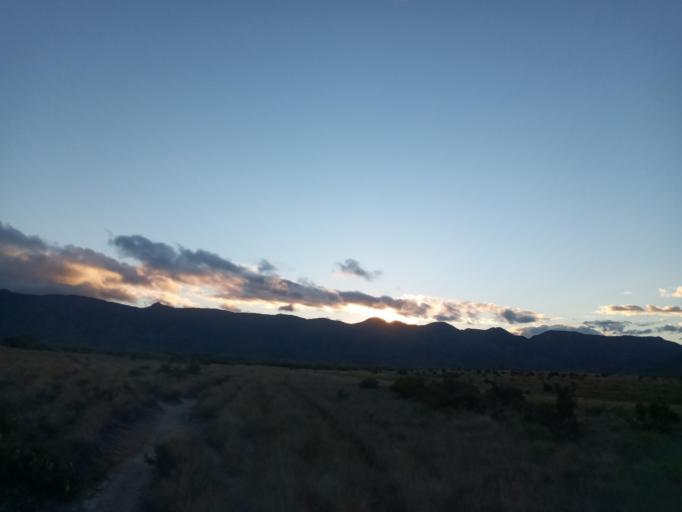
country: MG
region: Anosy
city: Fort Dauphin
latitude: -24.5129
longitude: 47.2295
